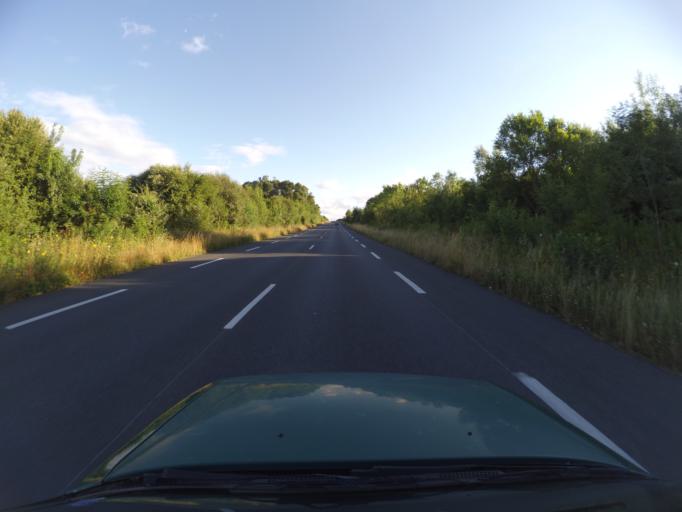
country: FR
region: Pays de la Loire
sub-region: Departement de la Vendee
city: Saint-Hilaire-de-Loulay
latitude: 46.9905
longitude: -1.3516
